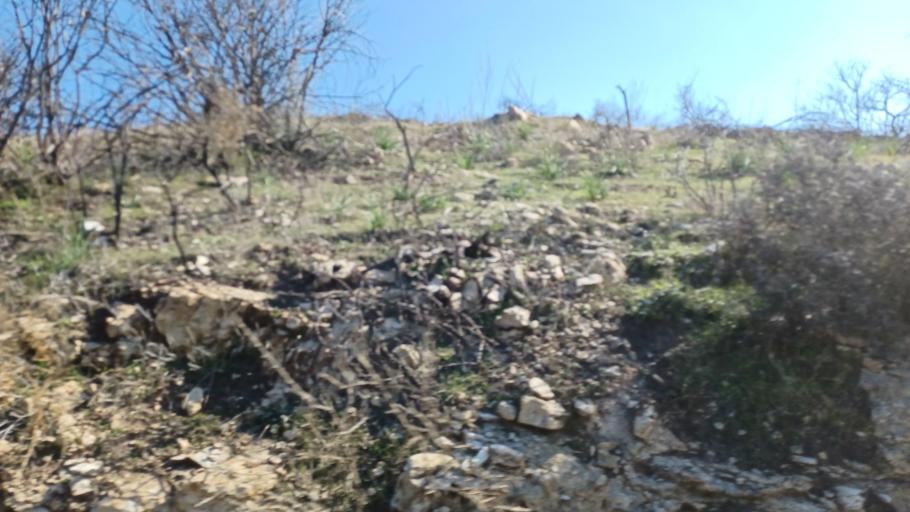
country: CY
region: Limassol
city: Pachna
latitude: 34.8106
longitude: 32.6639
